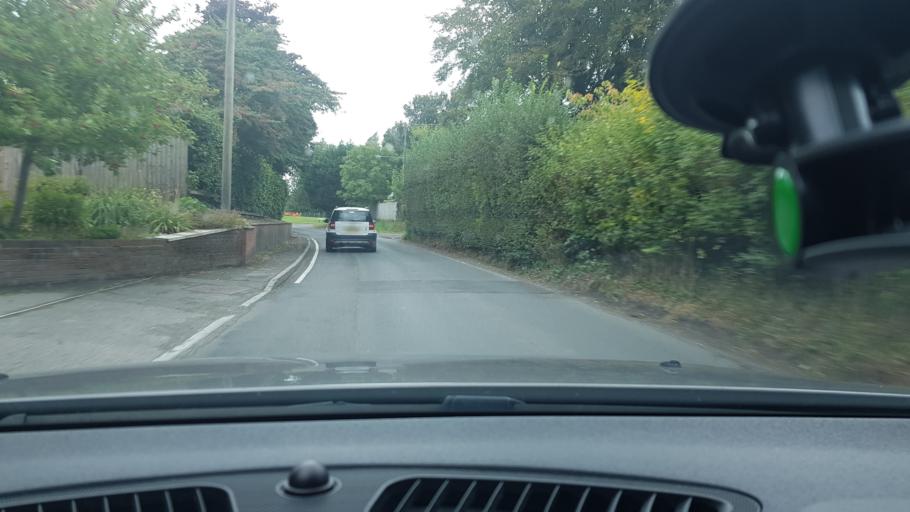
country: GB
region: England
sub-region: Wiltshire
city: Burbage
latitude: 51.3436
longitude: -1.6334
